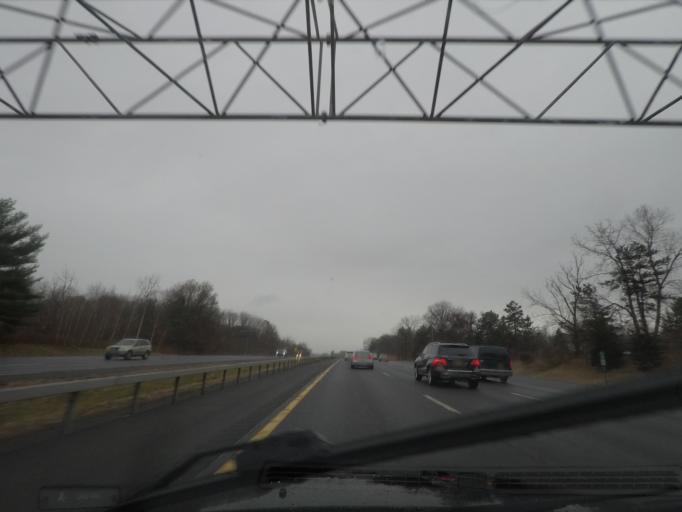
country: US
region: New York
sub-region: Albany County
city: West Albany
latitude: 42.6748
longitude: -73.7601
